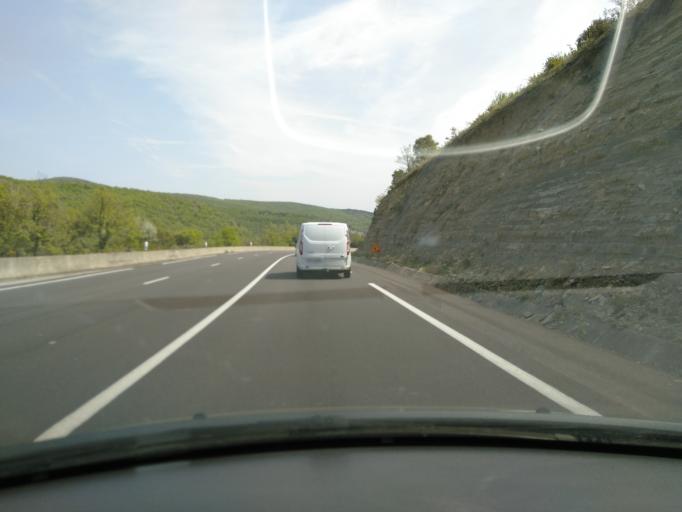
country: FR
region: Rhone-Alpes
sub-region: Departement de l'Ardeche
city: Alba-la-Romaine
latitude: 44.5679
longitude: 4.6354
